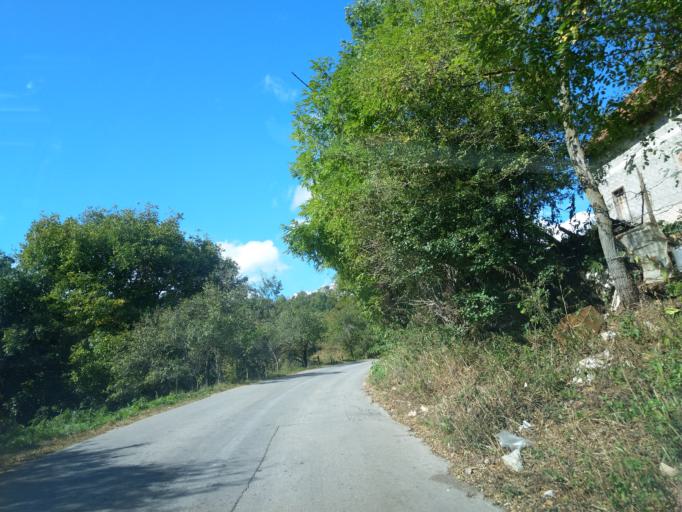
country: RS
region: Central Serbia
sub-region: Zlatiborski Okrug
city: Cajetina
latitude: 43.7137
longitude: 19.8337
